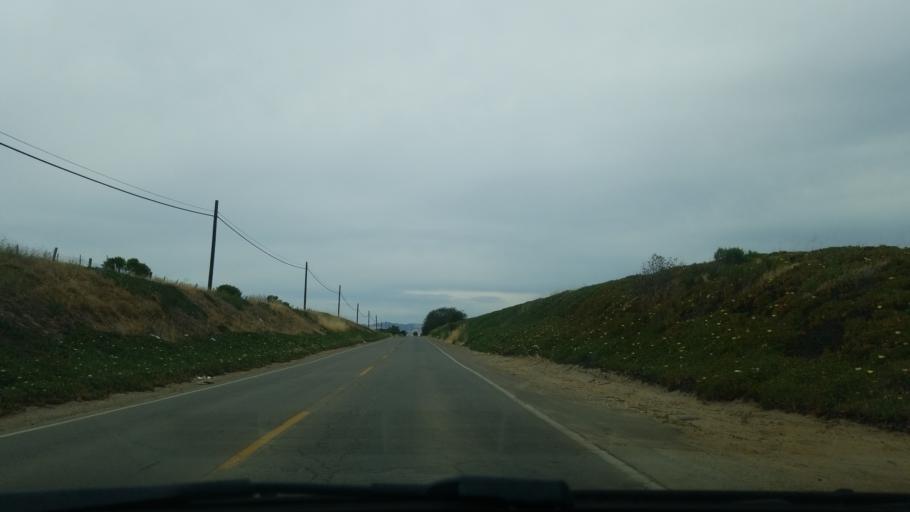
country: US
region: California
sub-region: Santa Barbara County
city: Santa Maria
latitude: 34.9135
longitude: -120.4847
